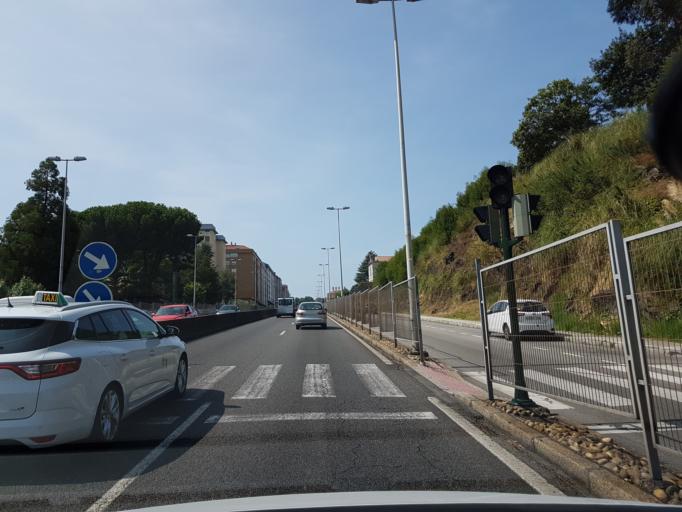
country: ES
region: Galicia
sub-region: Provincia de Pontevedra
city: Vigo
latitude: 42.2250
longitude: -8.7121
